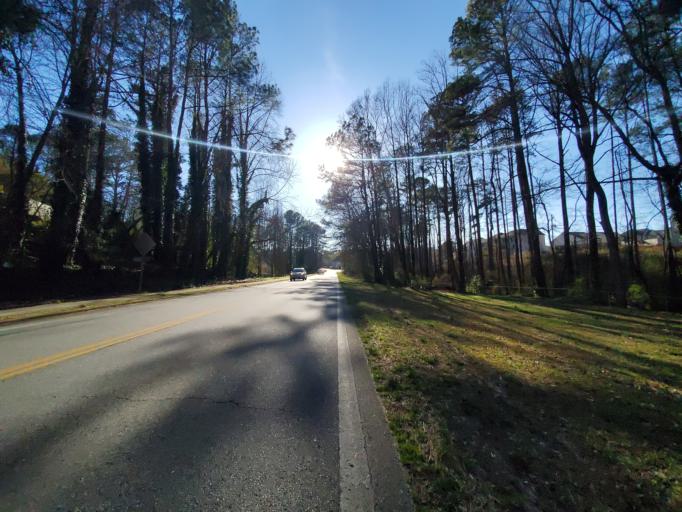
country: US
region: Georgia
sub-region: Gwinnett County
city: Lilburn
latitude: 33.8839
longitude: -84.1059
